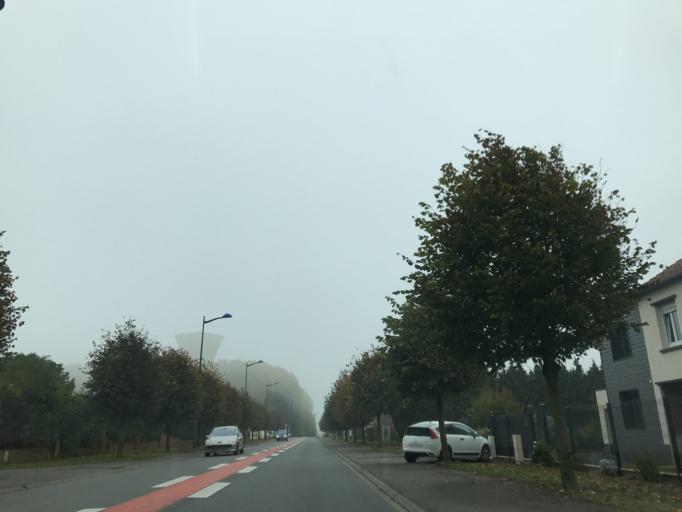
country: FR
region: Nord-Pas-de-Calais
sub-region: Departement du Pas-de-Calais
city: Bapaume
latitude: 50.0934
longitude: 2.8637
